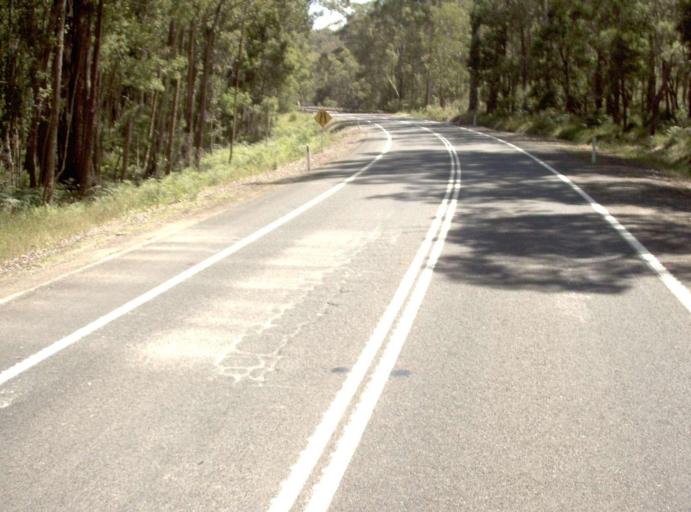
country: AU
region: New South Wales
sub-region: Bombala
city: Bombala
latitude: -37.5622
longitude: 149.0663
